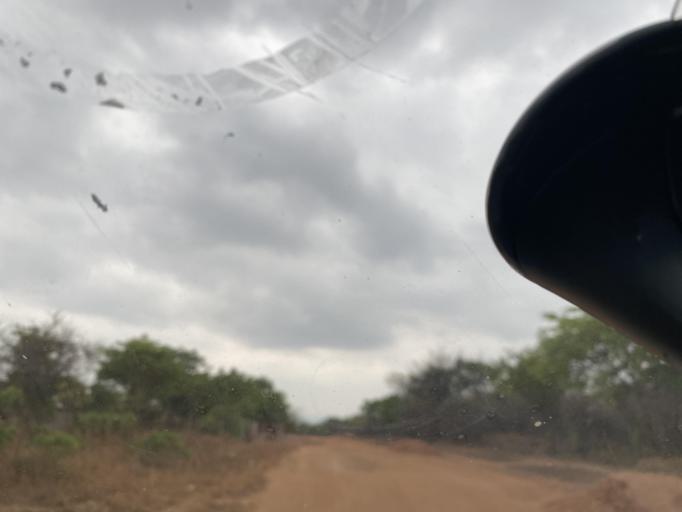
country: ZM
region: Lusaka
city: Chongwe
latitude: -15.2704
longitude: 28.7316
